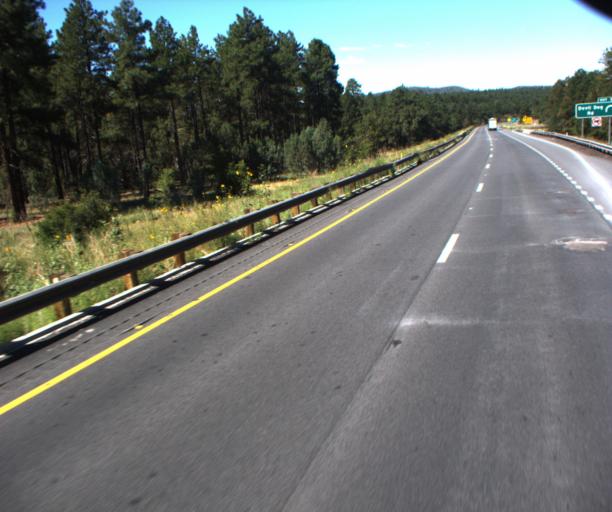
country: US
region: Arizona
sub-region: Coconino County
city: Williams
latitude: 35.2215
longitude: -112.2750
